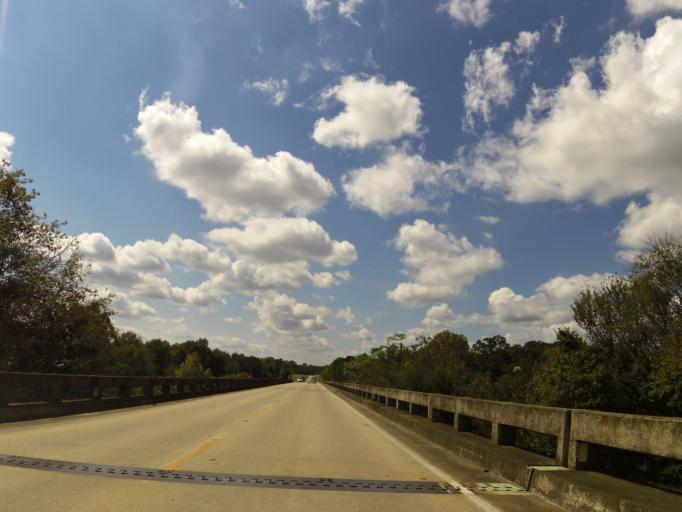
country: US
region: Alabama
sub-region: Dallas County
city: Selma
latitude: 32.3600
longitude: -87.1335
